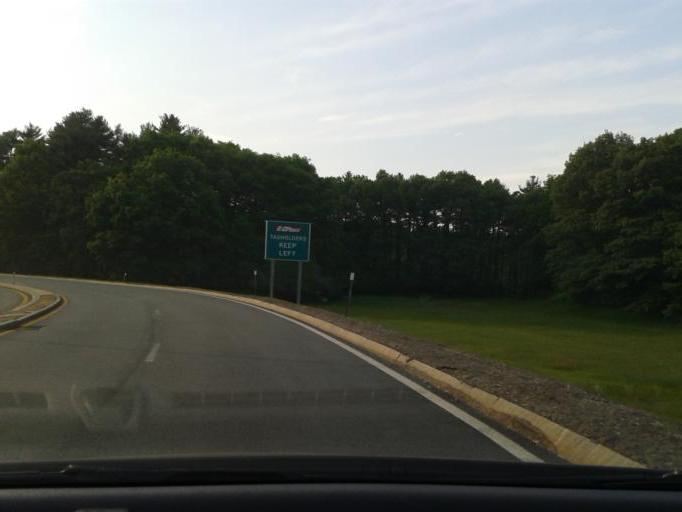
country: US
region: Massachusetts
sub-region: Middlesex County
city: Cochituate
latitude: 42.3140
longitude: -71.3818
